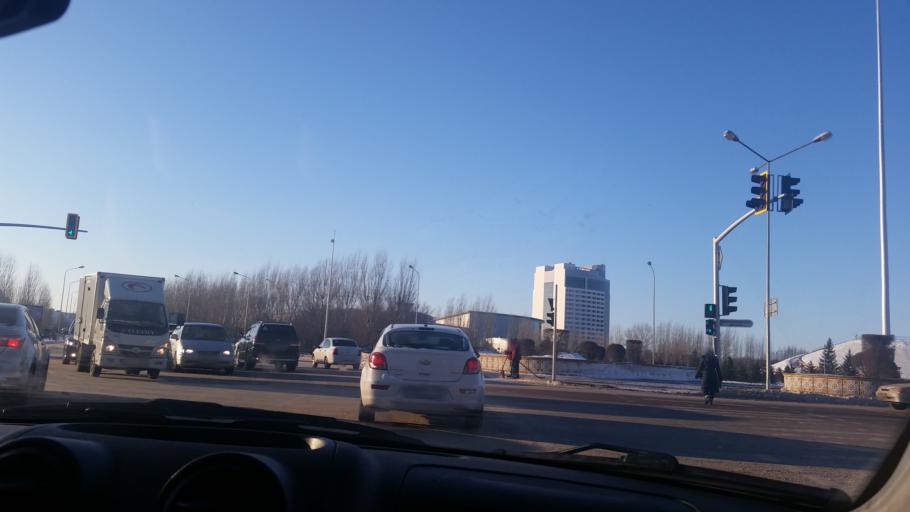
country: KZ
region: Astana Qalasy
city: Astana
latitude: 51.1471
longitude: 71.4229
